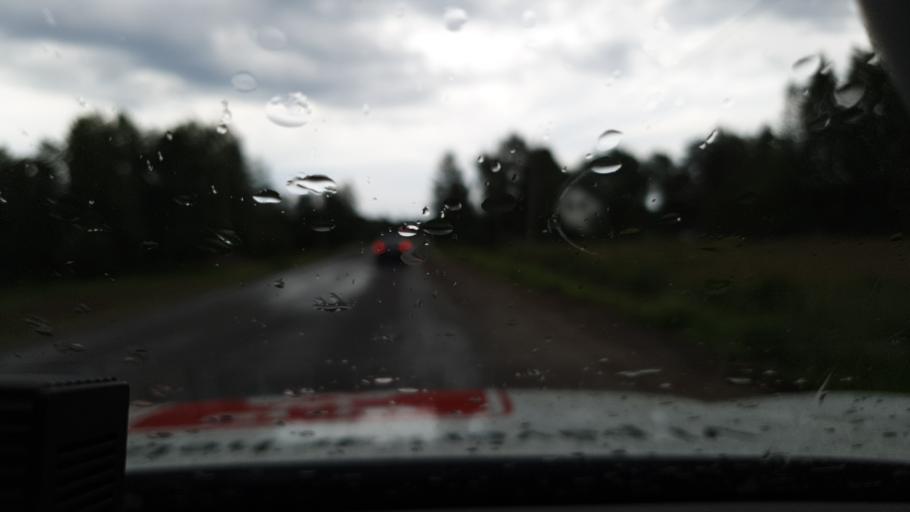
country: SE
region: Norrbotten
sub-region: Bodens Kommun
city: Boden
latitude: 65.8525
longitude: 21.5013
